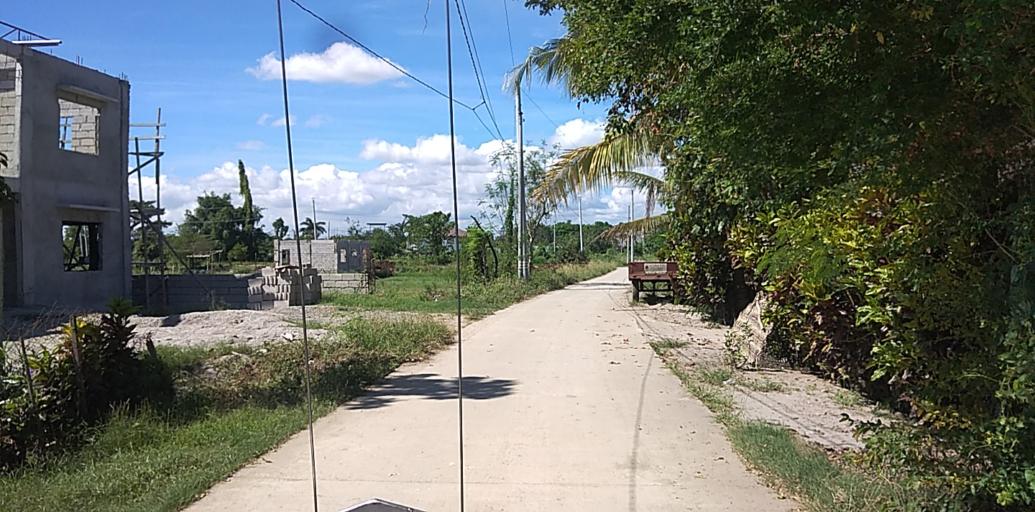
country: PH
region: Central Luzon
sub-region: Province of Pampanga
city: Arayat
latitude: 15.1271
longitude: 120.7828
